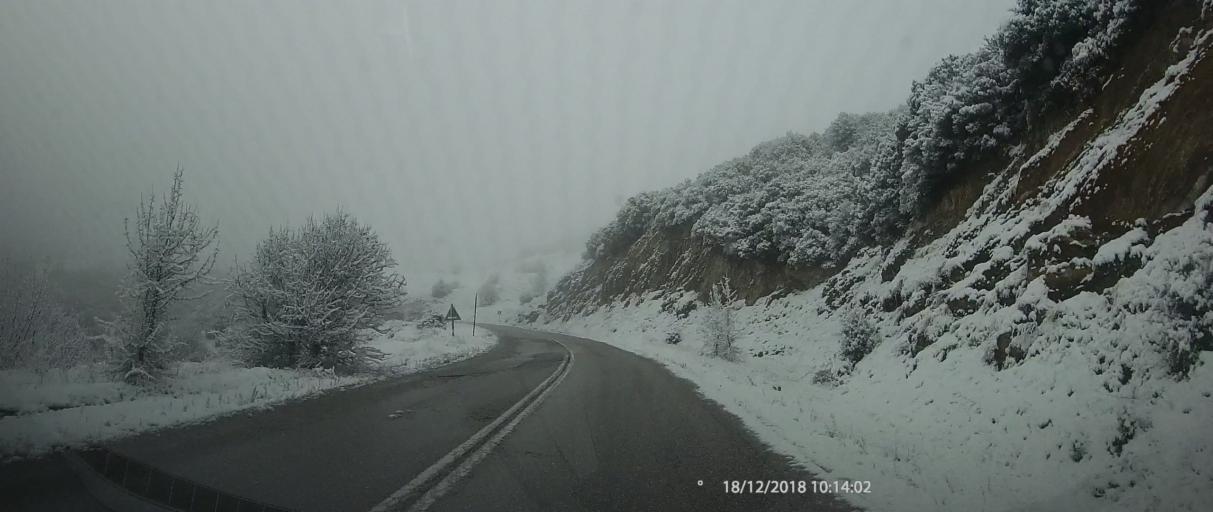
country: GR
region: Thessaly
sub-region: Nomos Larisis
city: Livadi
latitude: 40.1062
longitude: 22.2057
